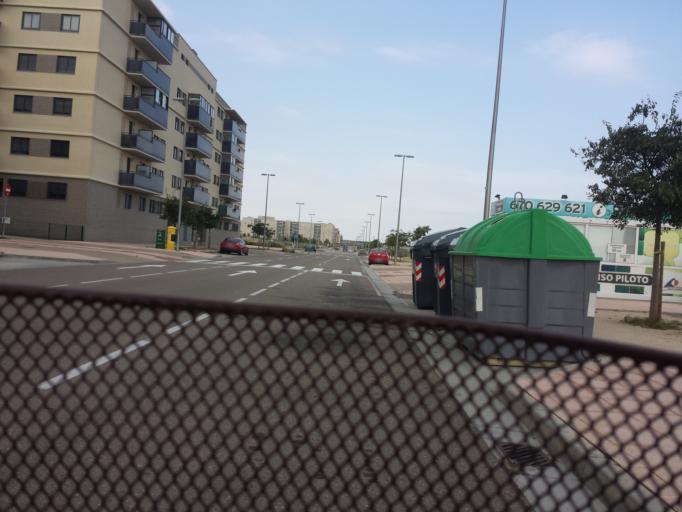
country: ES
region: Aragon
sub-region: Provincia de Zaragoza
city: Montecanal
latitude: 41.6240
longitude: -0.9522
